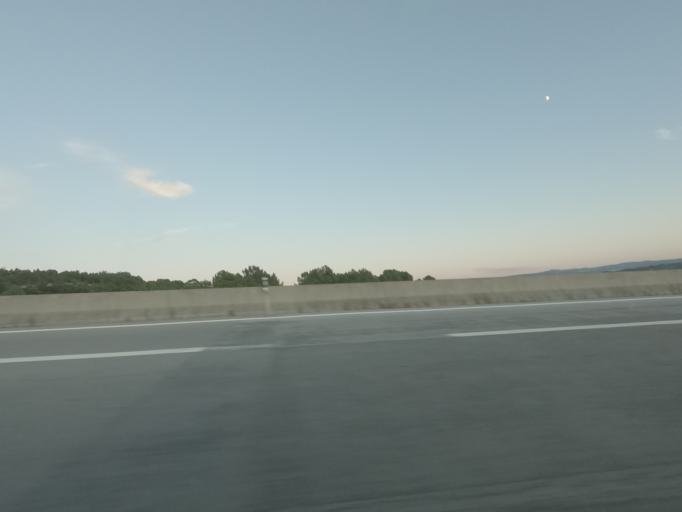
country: PT
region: Vila Real
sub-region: Vila Real
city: Vila Real
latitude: 41.2444
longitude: -7.7214
